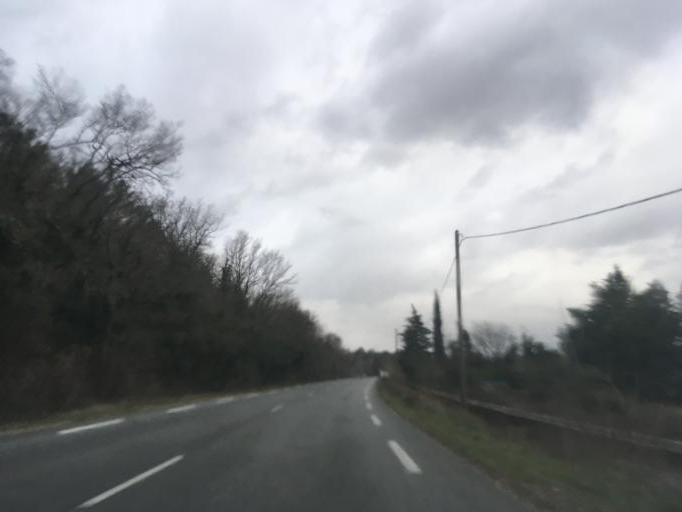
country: FR
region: Provence-Alpes-Cote d'Azur
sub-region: Departement du Var
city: Sainte-Anastasie-sur-Issole
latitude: 43.3396
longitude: 6.1316
